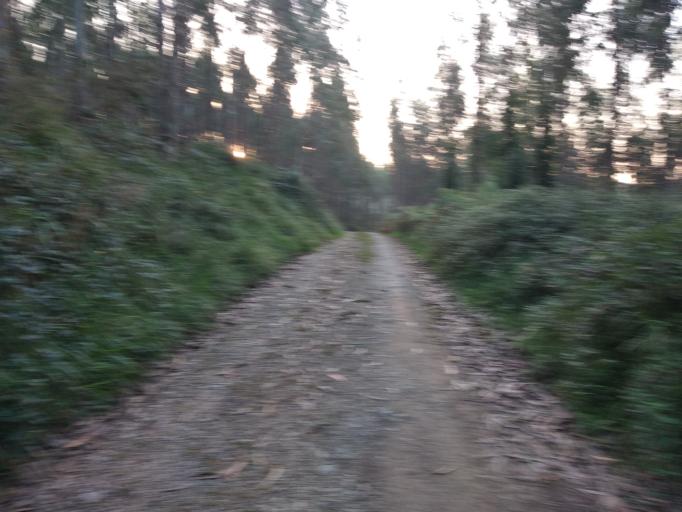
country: ES
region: Cantabria
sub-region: Provincia de Cantabria
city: Entrambasaguas
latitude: 43.3260
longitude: -3.6810
